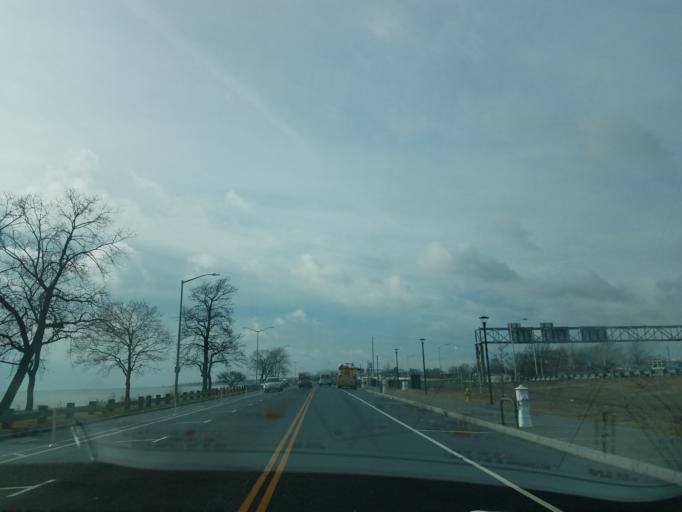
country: US
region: Connecticut
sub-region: New Haven County
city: New Haven
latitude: 41.2931
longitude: -72.9189
